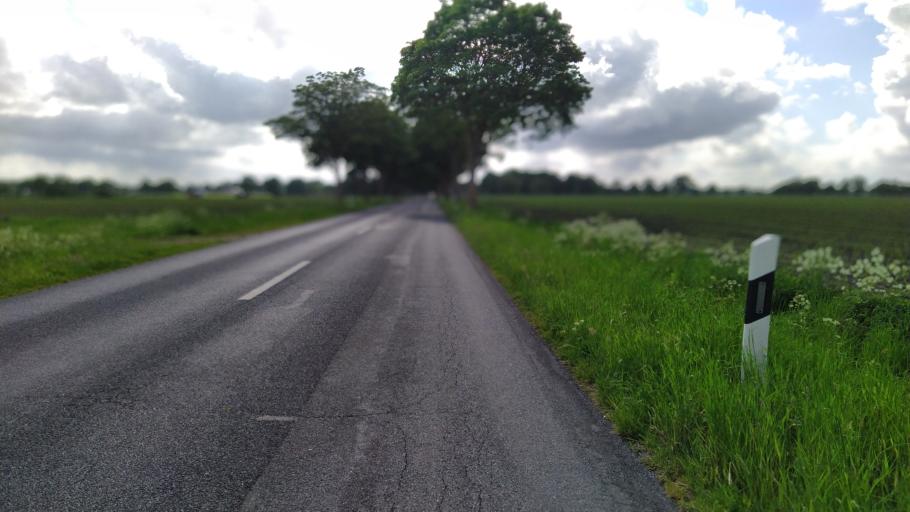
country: DE
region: Lower Saxony
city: Brest
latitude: 53.4528
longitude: 9.4009
